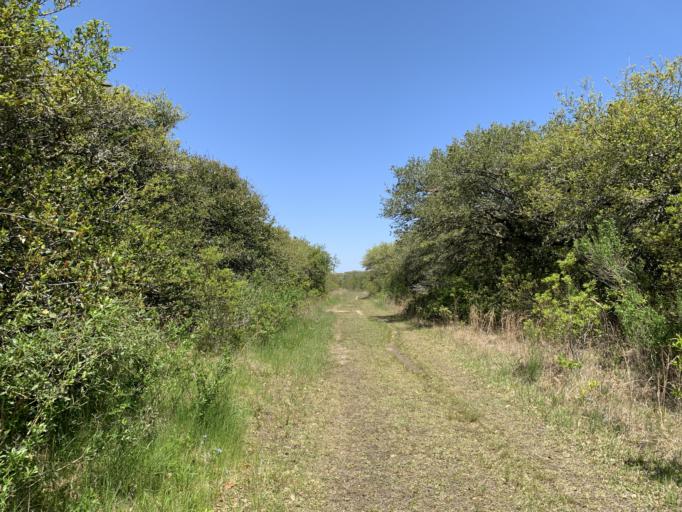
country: US
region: North Carolina
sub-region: Dare County
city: Southern Shores
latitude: 36.2356
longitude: -75.7775
